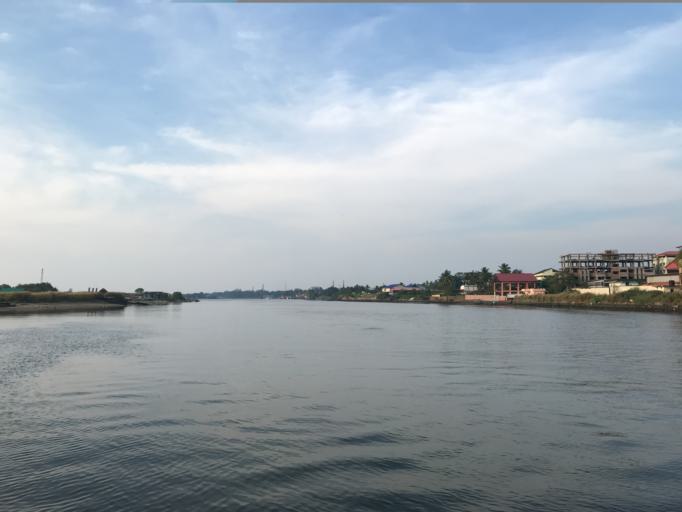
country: IN
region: Karnataka
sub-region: Dakshina Kannada
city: Mangalore
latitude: 12.8645
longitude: 74.8306
